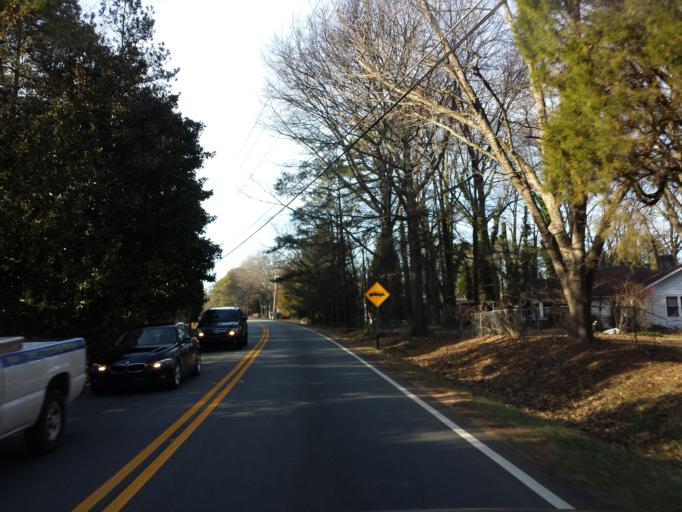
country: US
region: Georgia
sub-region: Cobb County
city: Kennesaw
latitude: 34.0435
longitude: -84.5526
